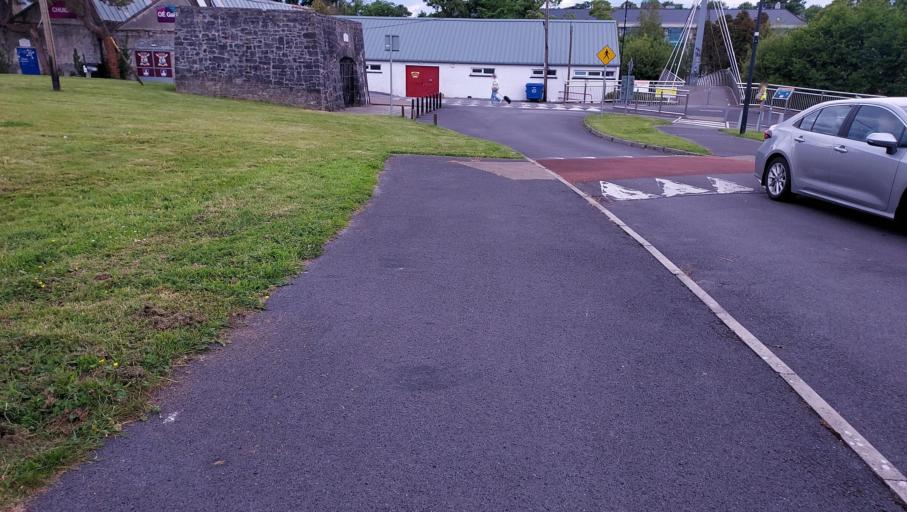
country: IE
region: Connaught
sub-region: County Galway
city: Gaillimh
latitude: 53.2773
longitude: -9.0571
